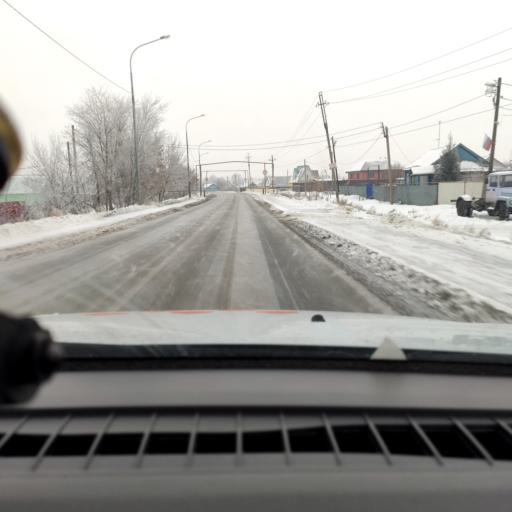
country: RU
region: Samara
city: Dubovyy Umet
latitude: 53.0765
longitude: 50.2099
